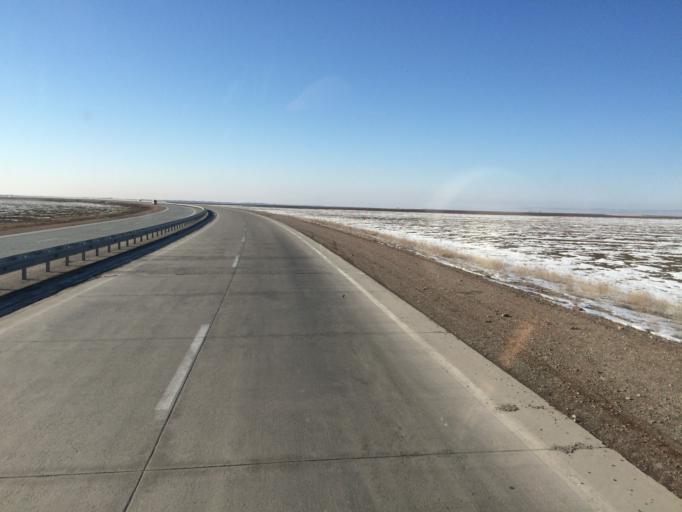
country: KG
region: Chuy
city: Sokuluk
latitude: 43.3463
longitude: 74.2992
